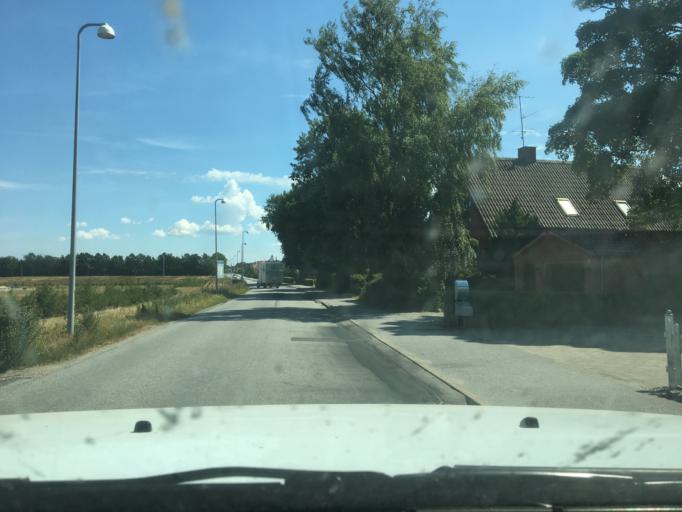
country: DK
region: Central Jutland
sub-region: Randers Kommune
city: Assentoft
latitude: 56.3649
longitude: 10.1552
